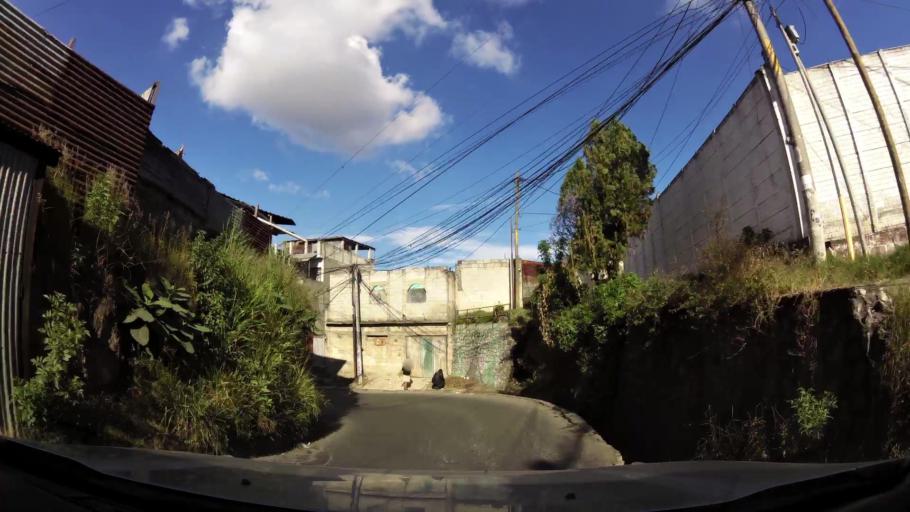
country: GT
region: Guatemala
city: Villa Nueva
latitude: 14.5263
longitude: -90.5773
